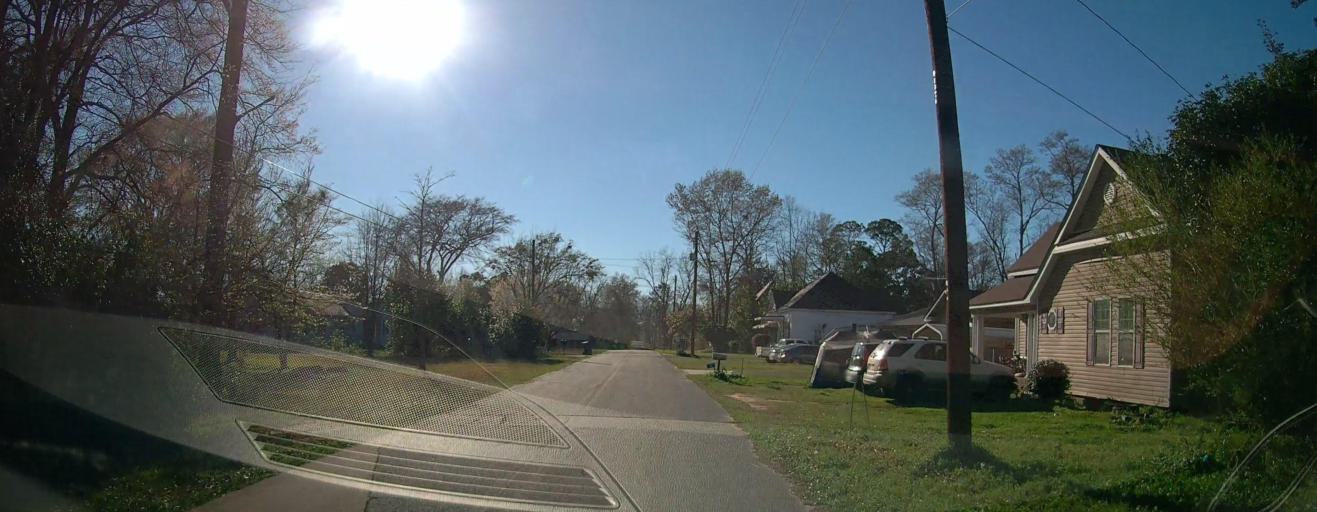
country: US
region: Georgia
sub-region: Taylor County
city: Reynolds
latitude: 32.5550
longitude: -84.0904
